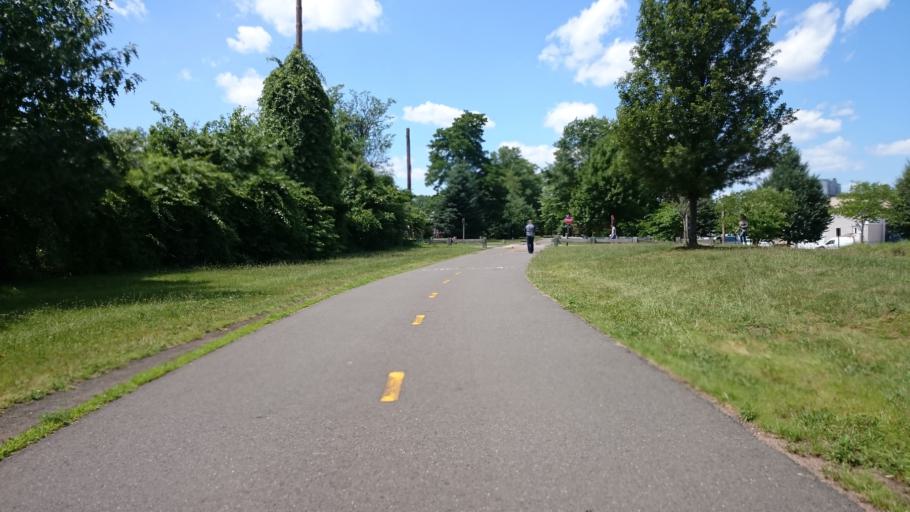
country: US
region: Connecticut
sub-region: New Haven County
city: New Haven
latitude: 41.3233
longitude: -72.9304
